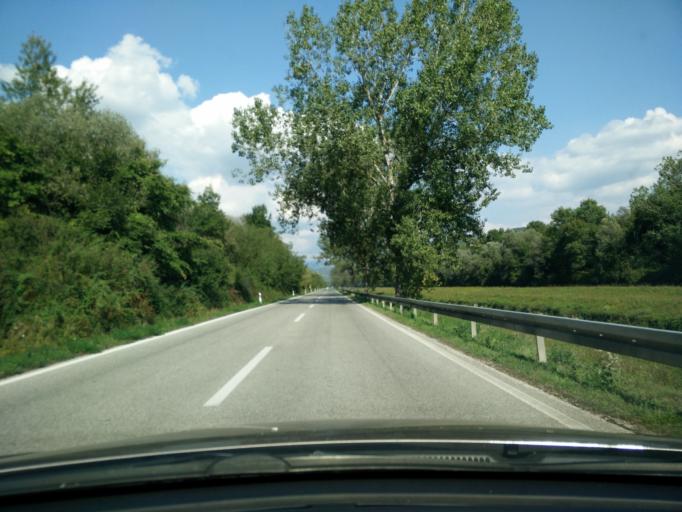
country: HR
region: Istarska
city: Karojba
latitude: 45.3486
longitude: 13.8445
